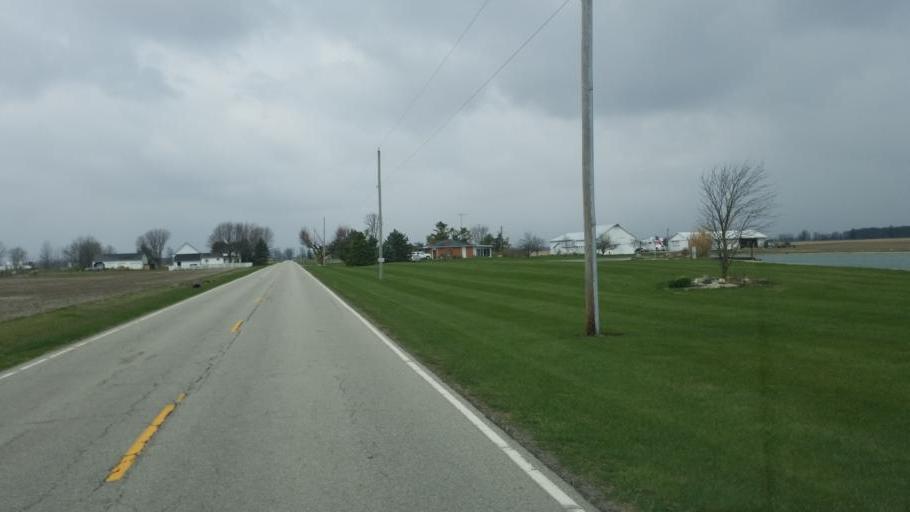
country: US
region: Ohio
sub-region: Union County
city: Richwood
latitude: 40.4260
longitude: -83.3450
